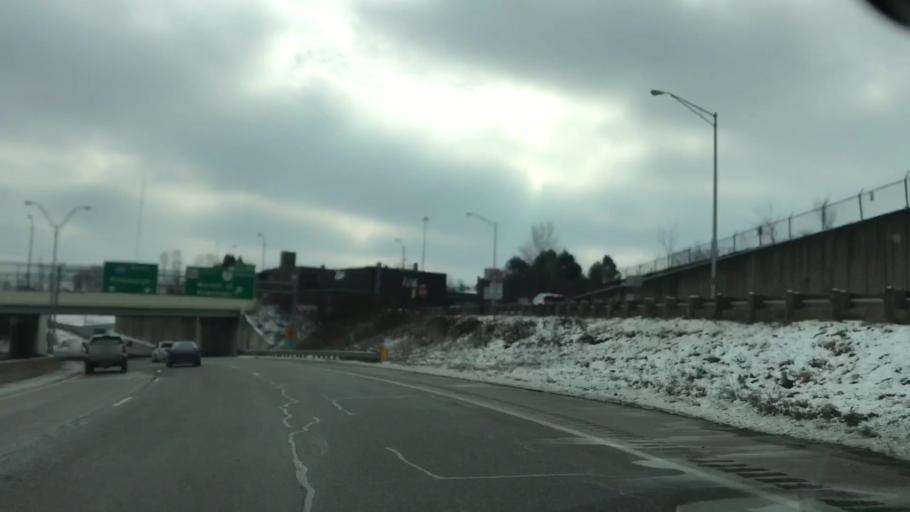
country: US
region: Ohio
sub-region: Mahoning County
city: Youngstown
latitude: 41.0933
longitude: -80.6559
